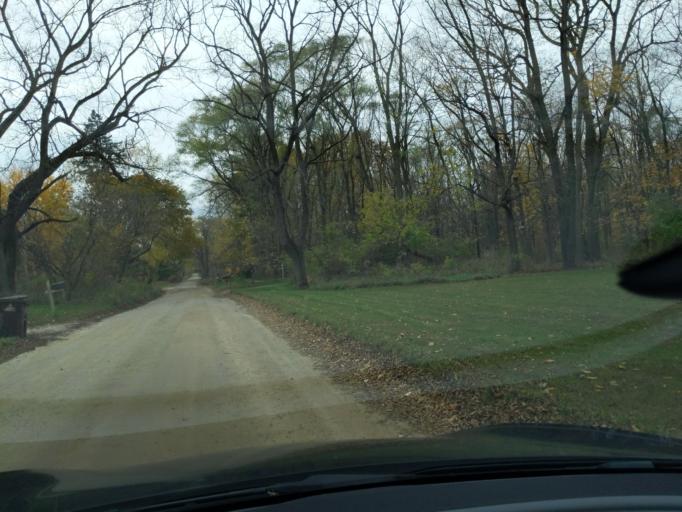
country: US
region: Michigan
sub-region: Eaton County
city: Eaton Rapids
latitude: 42.5531
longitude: -84.6116
